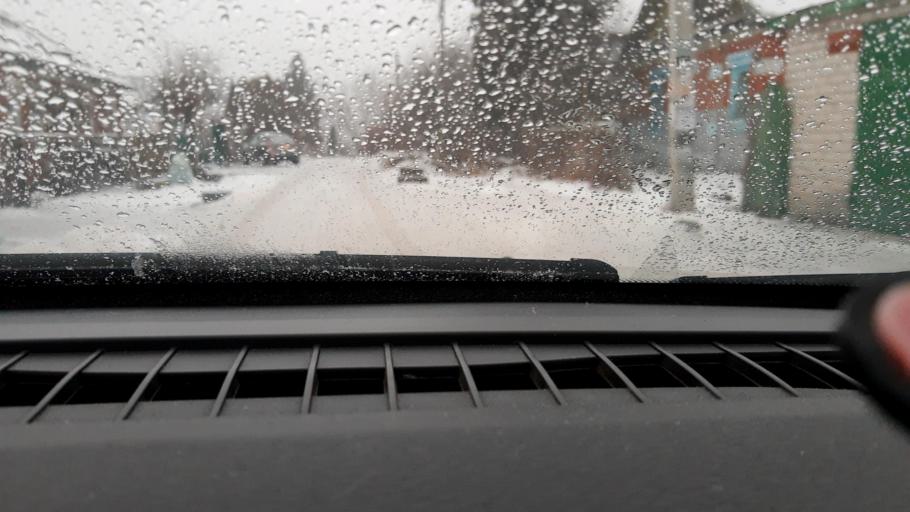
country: RU
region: Nizjnij Novgorod
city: Nizhniy Novgorod
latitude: 56.2510
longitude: 43.9990
